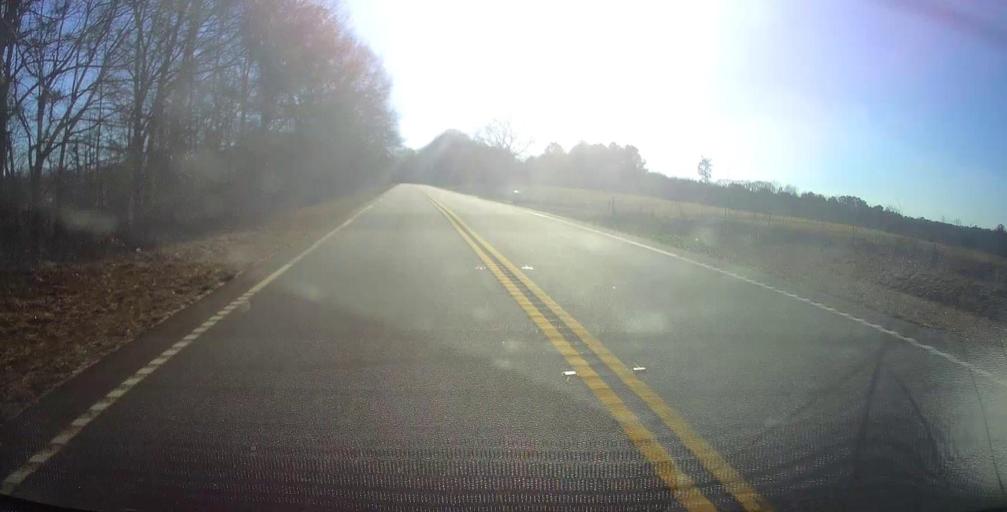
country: US
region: Georgia
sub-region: Meriwether County
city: Manchester
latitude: 32.9125
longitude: -84.6726
